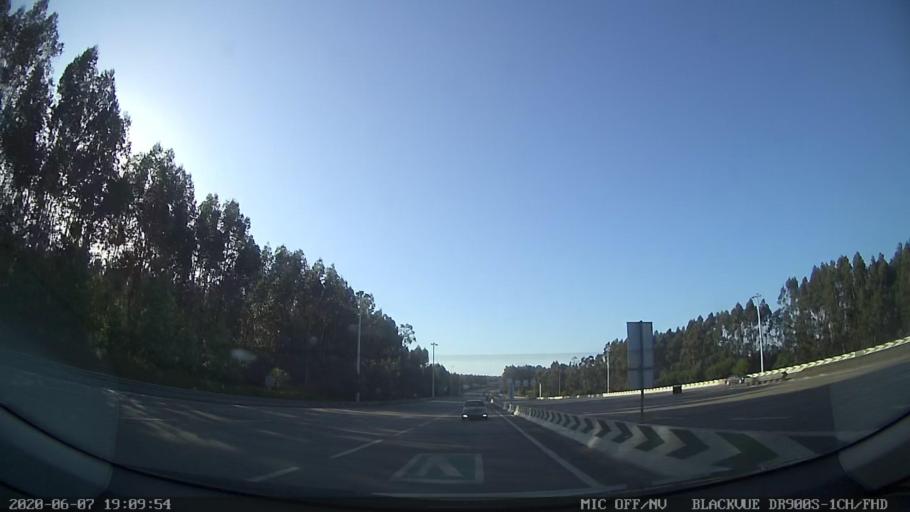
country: PT
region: Porto
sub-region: Maia
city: Nogueira
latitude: 41.2451
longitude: -8.5663
